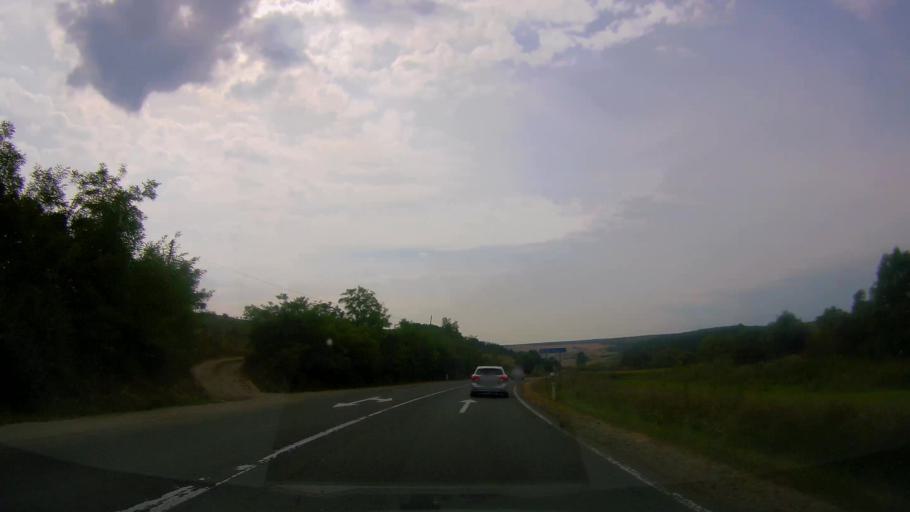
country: RO
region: Cluj
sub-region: Comuna Sanpaul
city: Sanpaul
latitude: 46.8541
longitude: 23.4066
